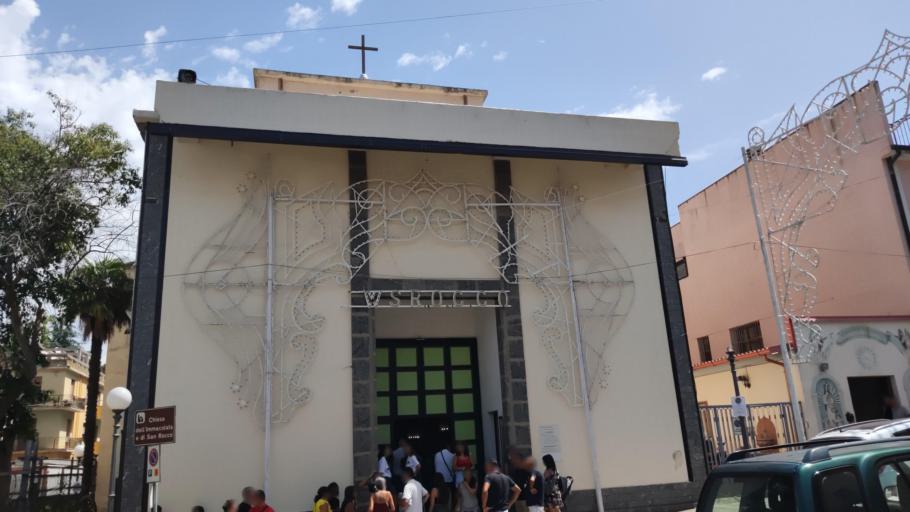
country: IT
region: Calabria
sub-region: Provincia di Reggio Calabria
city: Seminara
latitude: 38.3575
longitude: 15.8484
